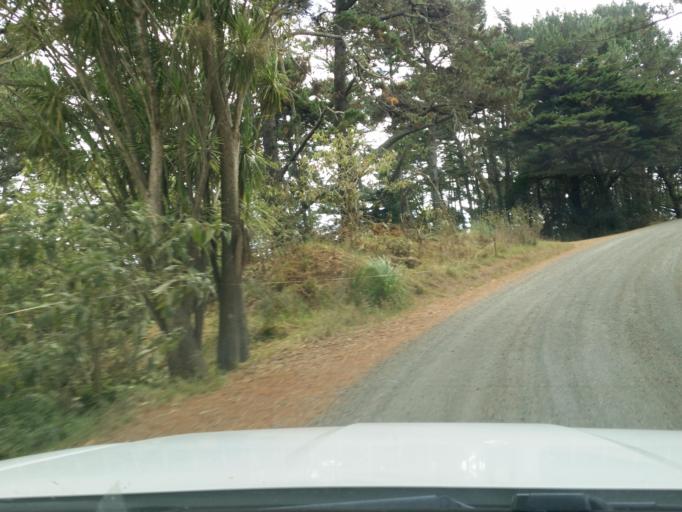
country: NZ
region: Auckland
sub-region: Auckland
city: Wellsford
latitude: -36.3137
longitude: 174.1300
